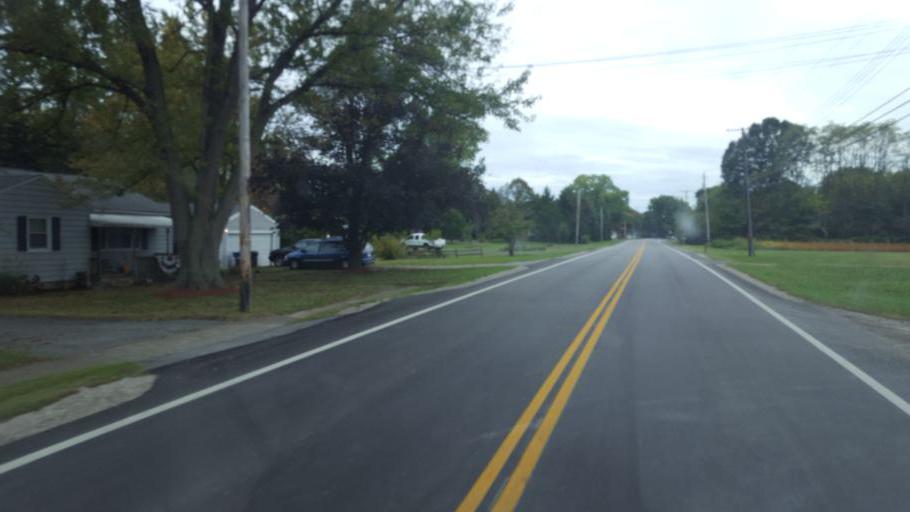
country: US
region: Ohio
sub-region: Lorain County
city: South Amherst
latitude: 41.3545
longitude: -82.2573
